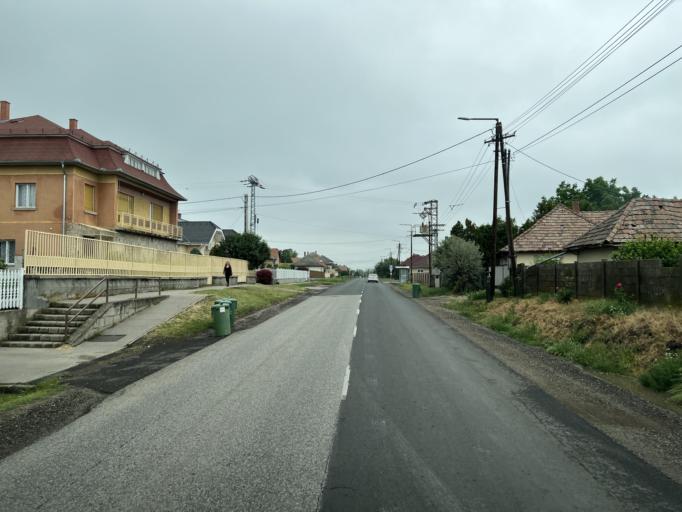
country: HU
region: Pest
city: Zsambok
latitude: 47.5470
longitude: 19.6045
